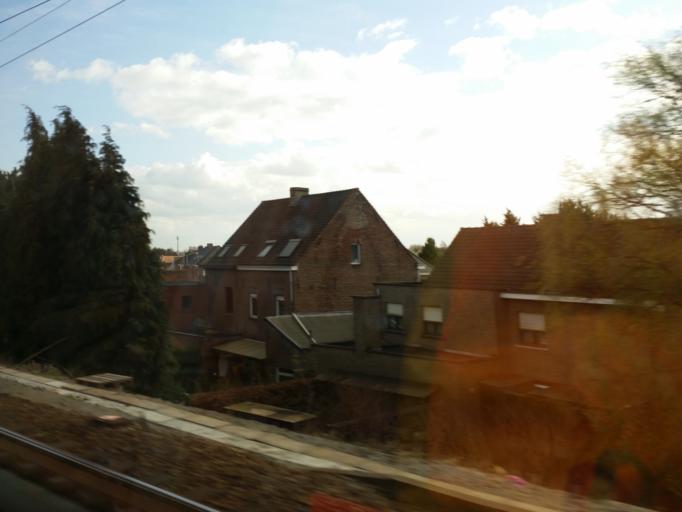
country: BE
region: Flanders
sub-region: Provincie Oost-Vlaanderen
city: Melle
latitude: 51.0016
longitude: 3.7992
